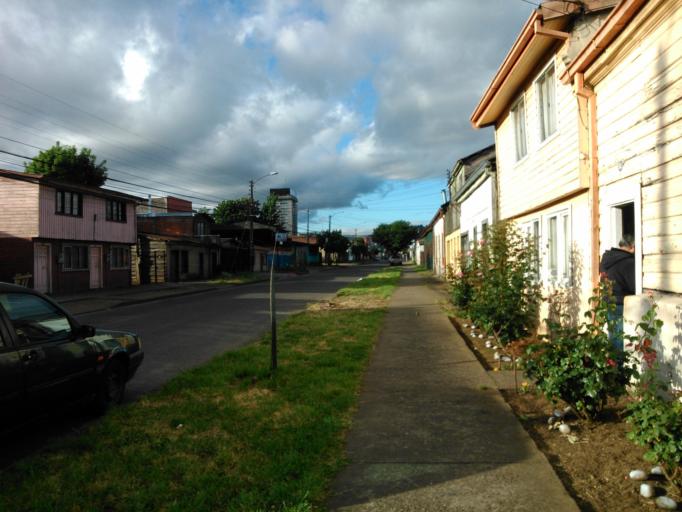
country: CL
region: Araucania
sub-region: Provincia de Cautin
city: Temuco
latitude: -38.7433
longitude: -72.5997
